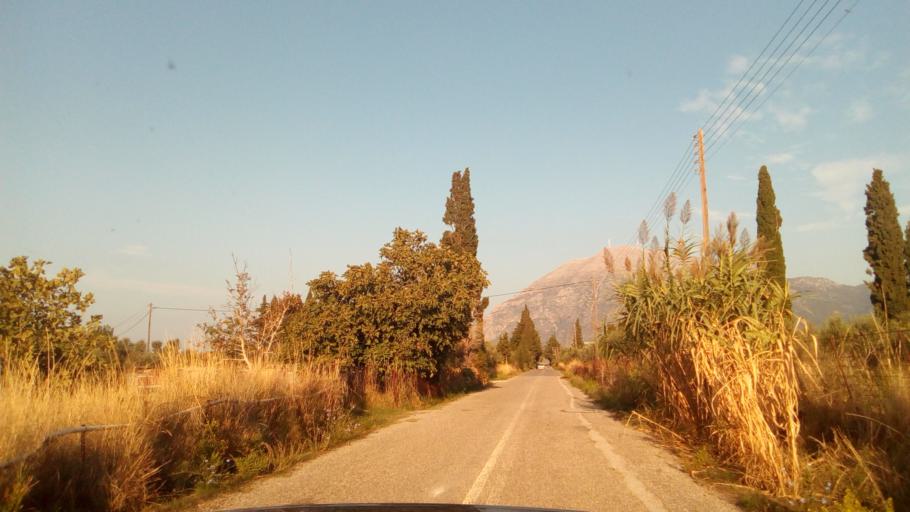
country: GR
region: West Greece
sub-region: Nomos Aitolias kai Akarnanias
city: Antirrio
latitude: 38.3356
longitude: 21.7508
